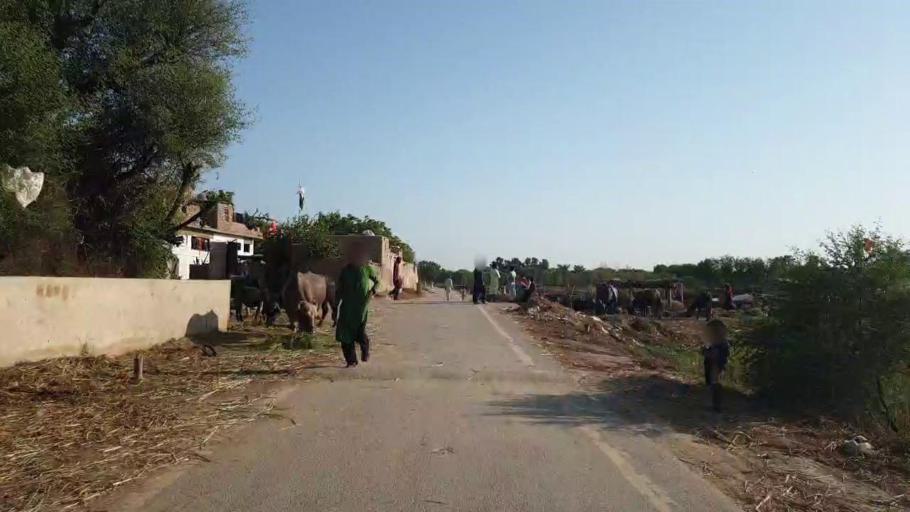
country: PK
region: Sindh
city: Hyderabad
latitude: 25.3478
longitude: 68.4156
